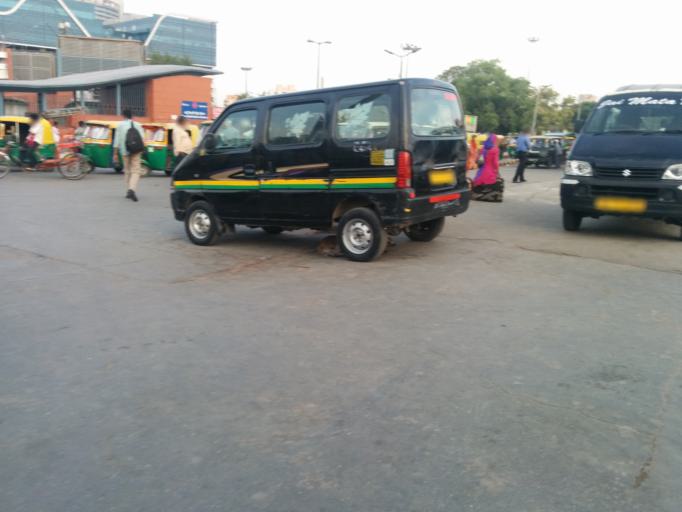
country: IN
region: NCT
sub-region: New Delhi
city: New Delhi
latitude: 28.6433
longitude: 77.2216
